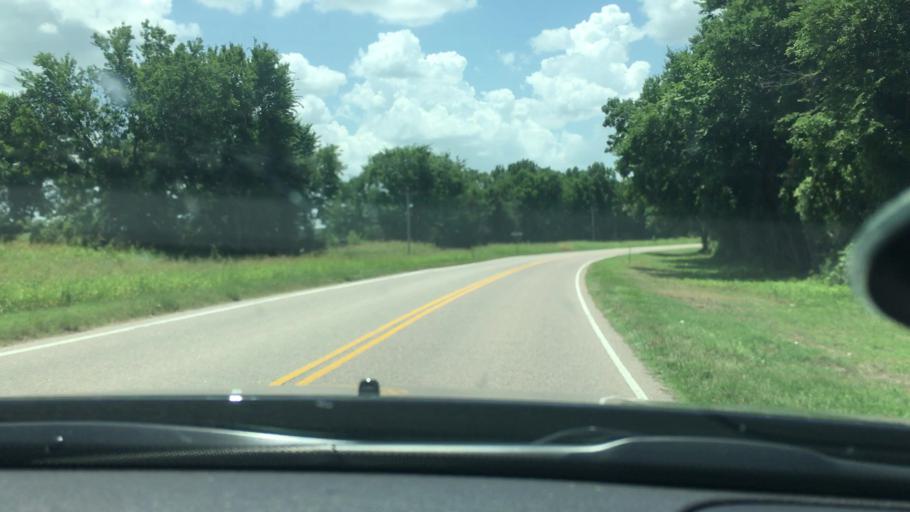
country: US
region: Oklahoma
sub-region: Johnston County
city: Tishomingo
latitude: 34.4841
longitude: -96.6267
